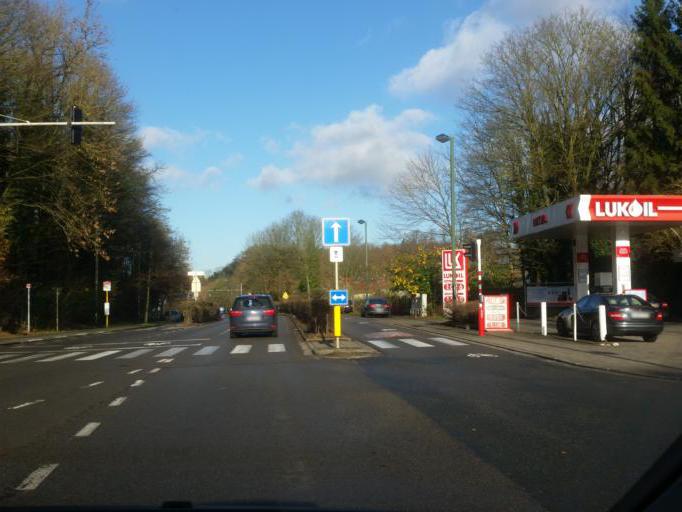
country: BE
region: Flanders
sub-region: Provincie Vlaams-Brabant
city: Hoeilaart
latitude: 50.7901
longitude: 4.4203
